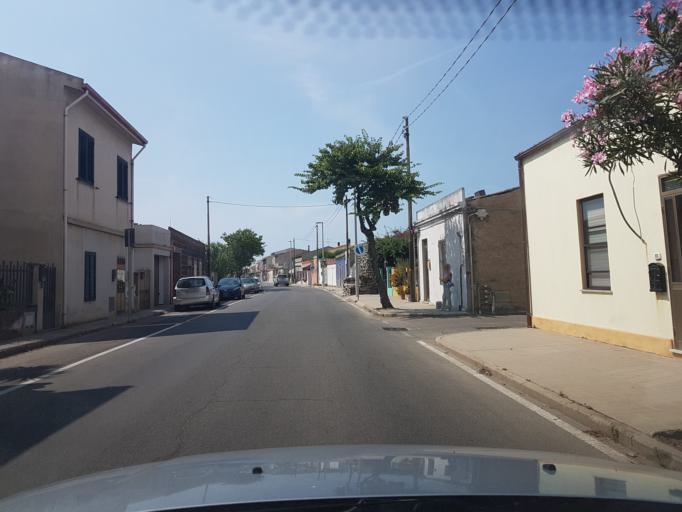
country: IT
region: Sardinia
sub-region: Provincia di Oristano
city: Cabras
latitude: 39.9246
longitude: 8.5383
